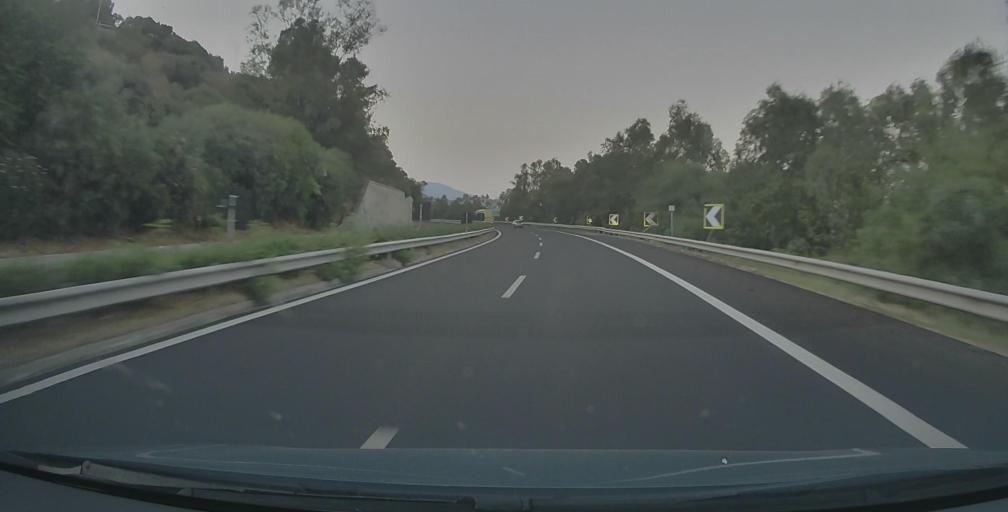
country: IT
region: Sicily
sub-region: Messina
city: Sant'Alessio Siculo
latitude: 37.9268
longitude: 15.3495
